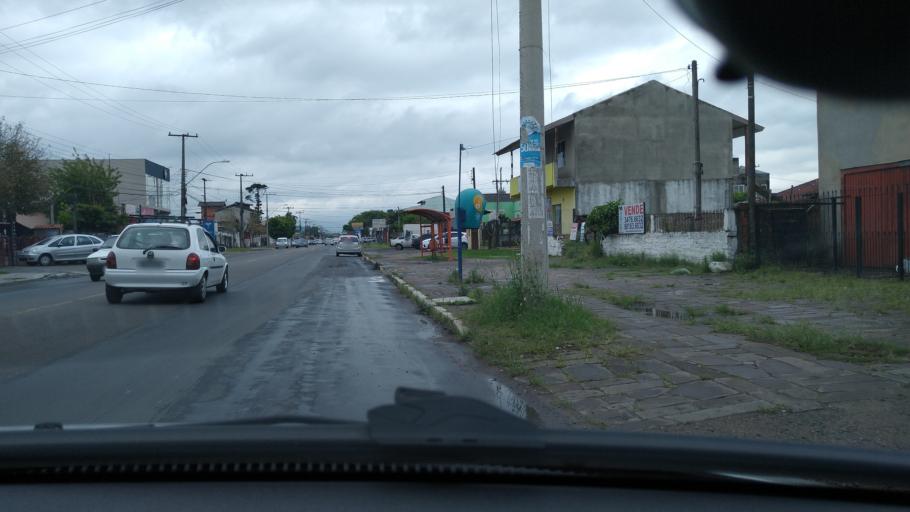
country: BR
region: Rio Grande do Sul
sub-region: Canoas
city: Canoas
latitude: -29.9015
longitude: -51.2127
